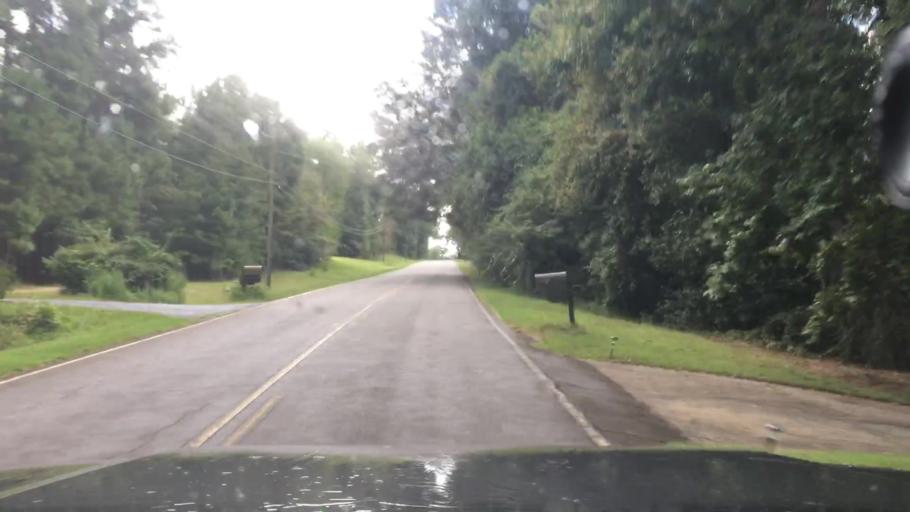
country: US
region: Georgia
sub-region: Bibb County
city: West Point
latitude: 32.8113
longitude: -83.7914
